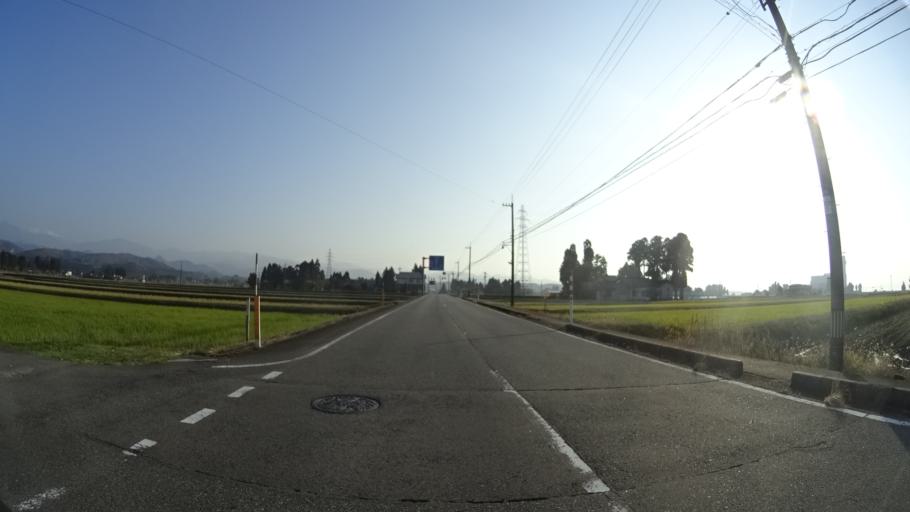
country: JP
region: Toyama
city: Kamiichi
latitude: 36.6269
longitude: 137.3158
